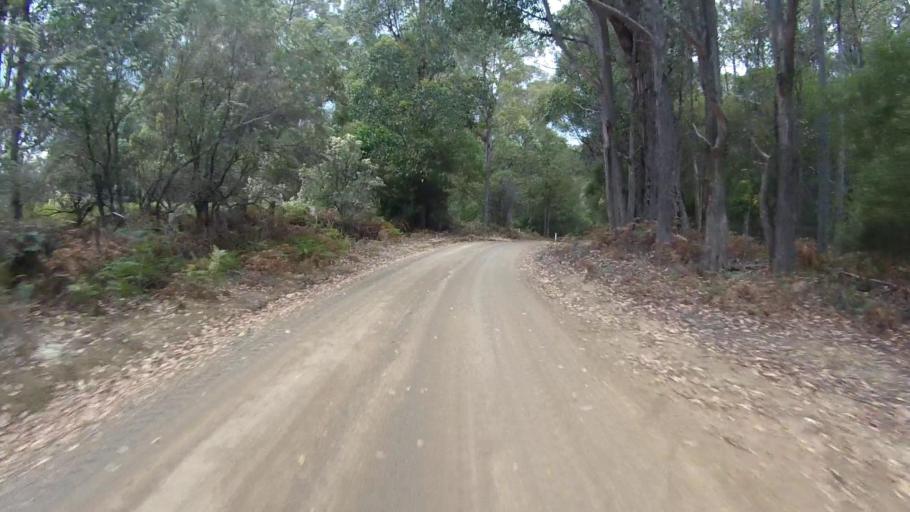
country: AU
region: Tasmania
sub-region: Huon Valley
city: Huonville
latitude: -42.9589
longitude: 147.0508
